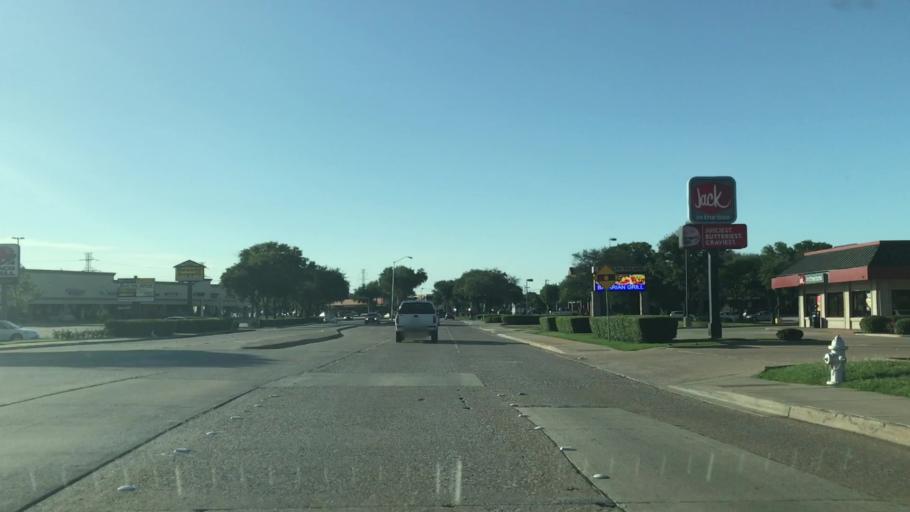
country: US
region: Texas
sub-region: Collin County
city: Plano
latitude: 33.0386
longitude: -96.7071
